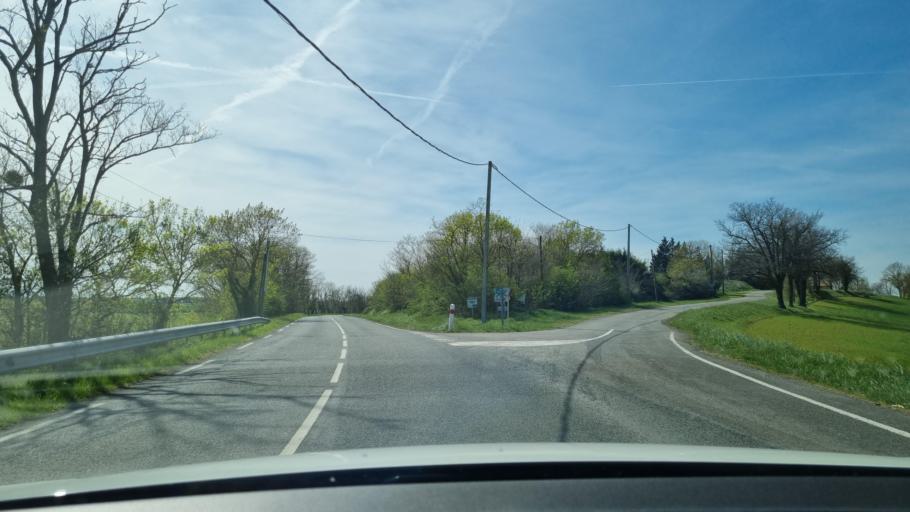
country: FR
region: Midi-Pyrenees
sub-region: Departement de la Haute-Garonne
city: Sainte-Foy-de-Peyrolieres
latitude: 43.4872
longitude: 1.0501
